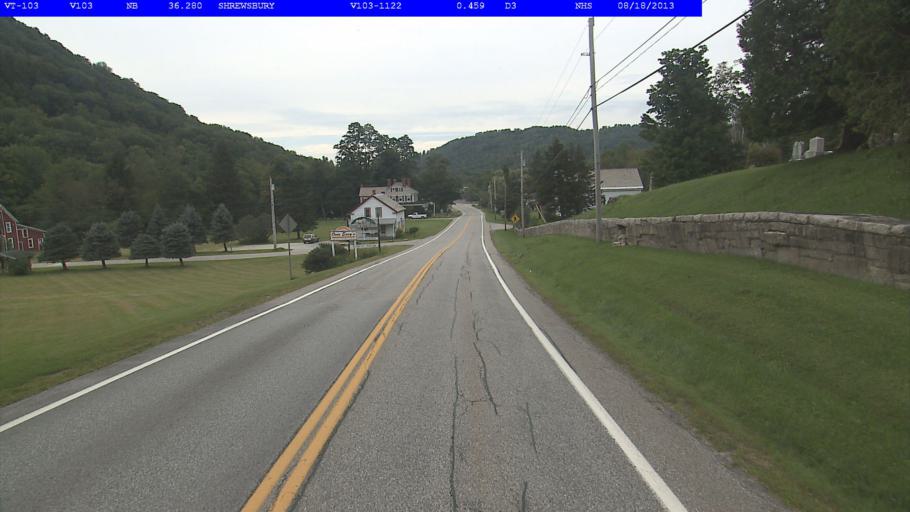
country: US
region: Vermont
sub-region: Rutland County
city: Rutland
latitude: 43.4797
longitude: -72.8949
